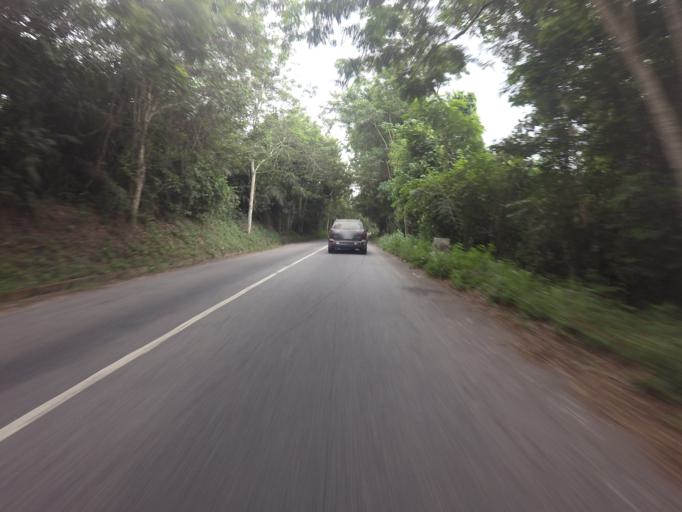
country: GH
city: Akropong
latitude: 5.9605
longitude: -0.1144
